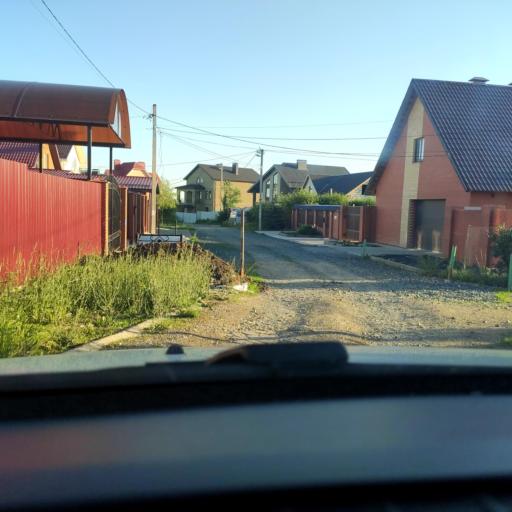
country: RU
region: Samara
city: Kinel'
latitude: 53.2746
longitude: 50.5907
